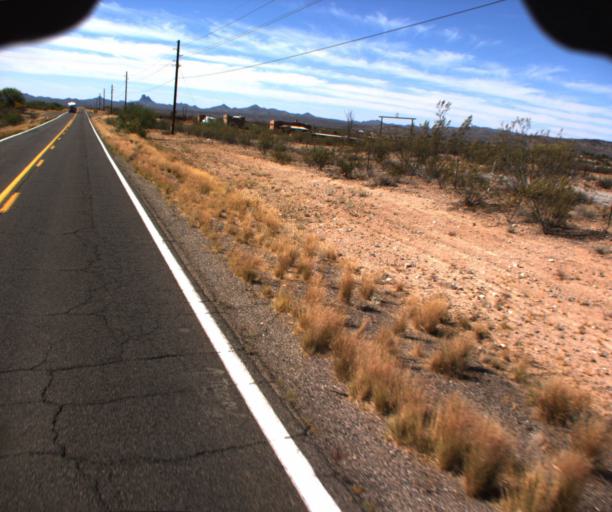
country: US
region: Arizona
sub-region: Maricopa County
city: Wickenburg
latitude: 34.0401
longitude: -112.8136
